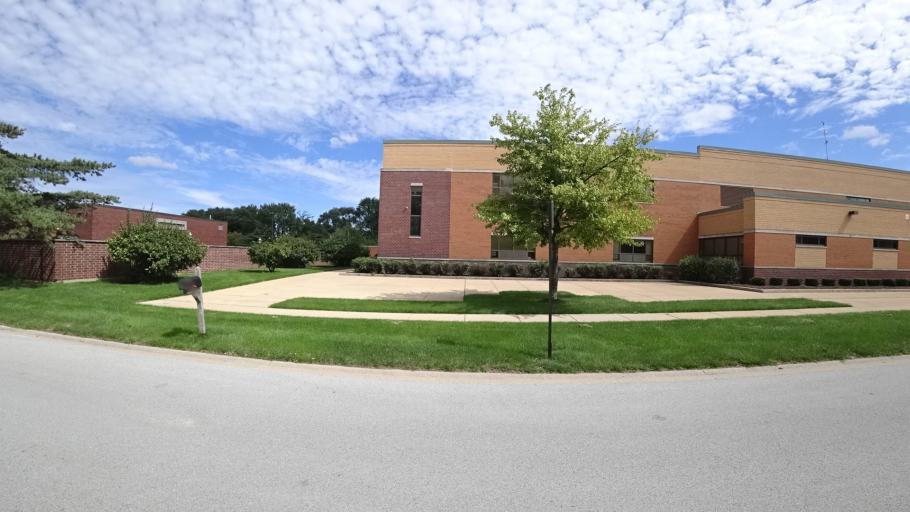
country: US
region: Illinois
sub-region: Cook County
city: Burbank
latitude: 41.7179
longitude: -87.7884
